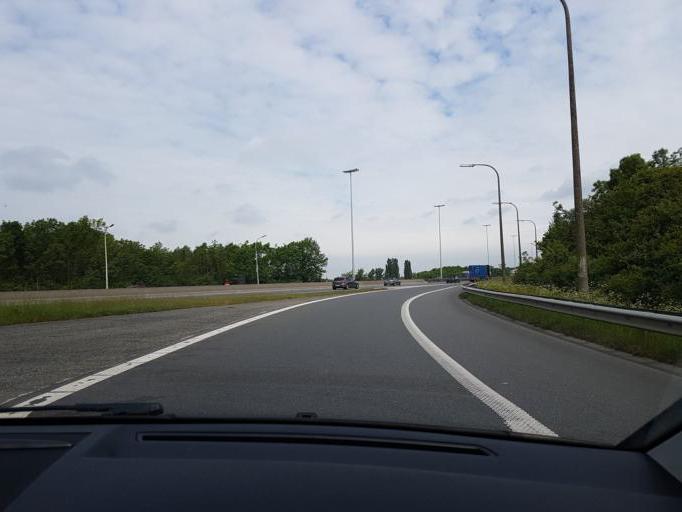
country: BE
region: Flanders
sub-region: Provincie Vlaams-Brabant
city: Dilbeek
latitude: 50.8653
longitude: 4.2709
